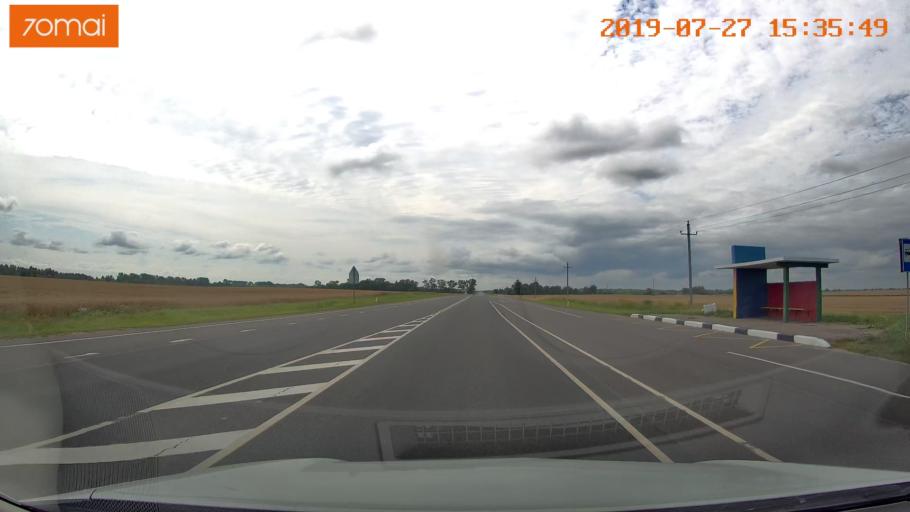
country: RU
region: Kaliningrad
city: Nesterov
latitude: 54.6130
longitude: 22.3867
